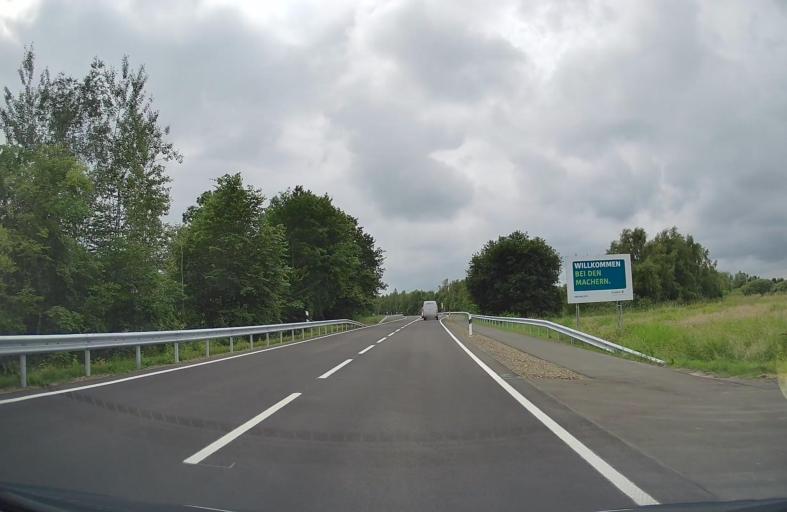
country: DE
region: Lower Saxony
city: Hilkenbrook
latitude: 53.0199
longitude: 7.7016
